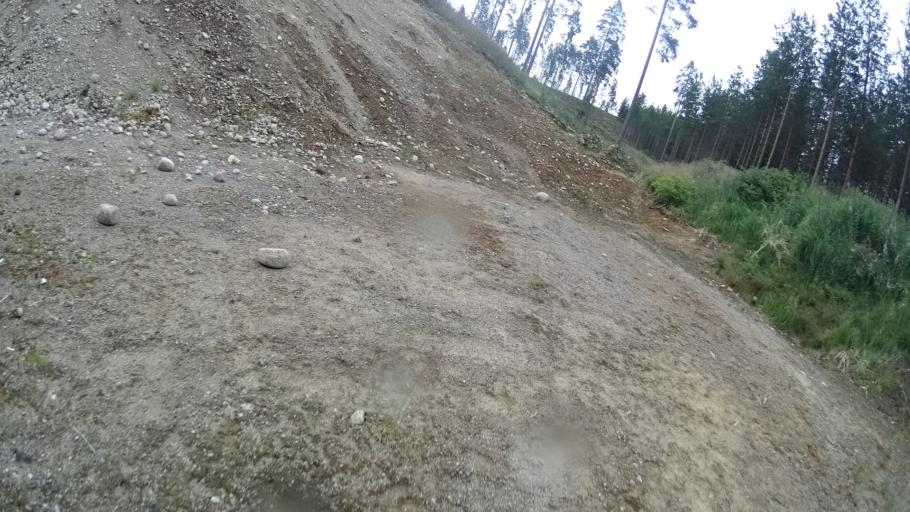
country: FI
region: Uusimaa
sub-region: Helsinki
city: Karkkila
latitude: 60.5954
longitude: 24.1807
